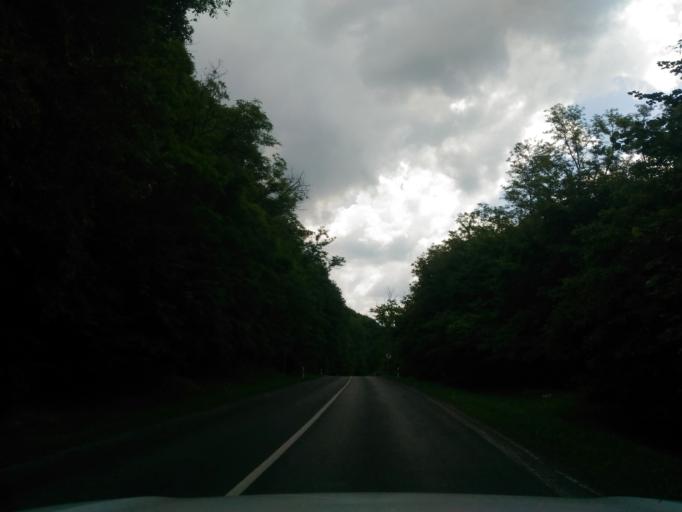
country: HU
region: Baranya
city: Komlo
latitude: 46.1774
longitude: 18.2101
